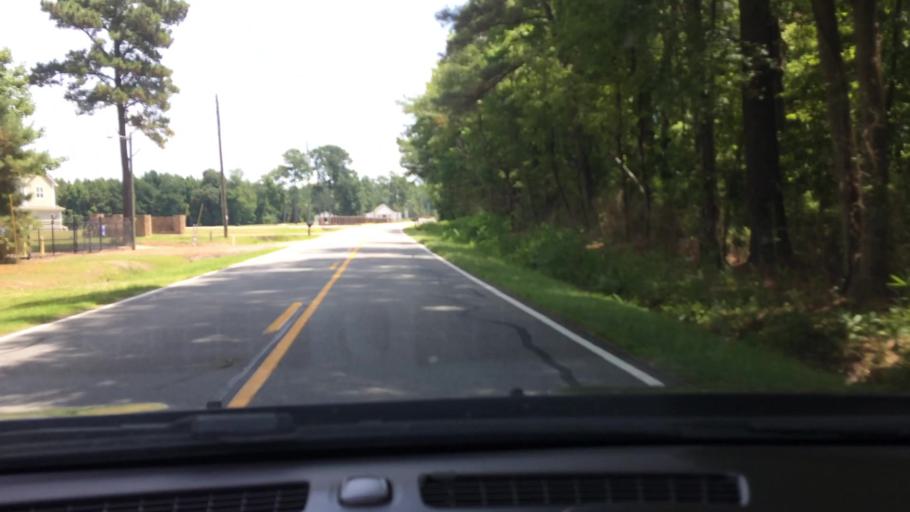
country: US
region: North Carolina
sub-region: Pitt County
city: Windsor
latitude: 35.4932
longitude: -77.3513
